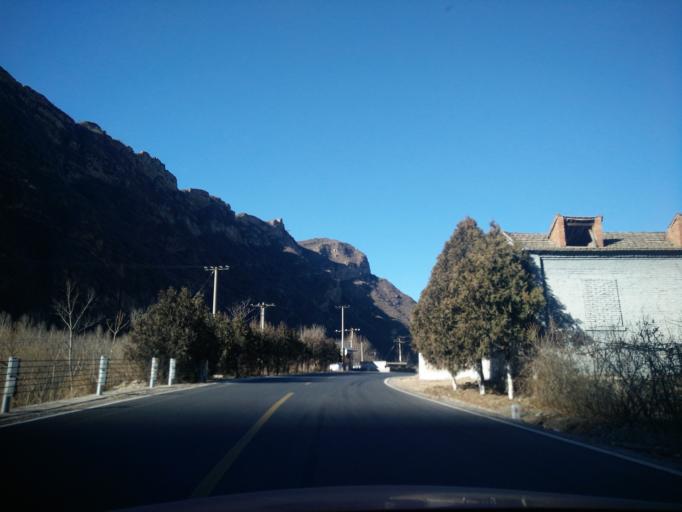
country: CN
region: Beijing
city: Yanchi
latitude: 40.0282
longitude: 115.8592
